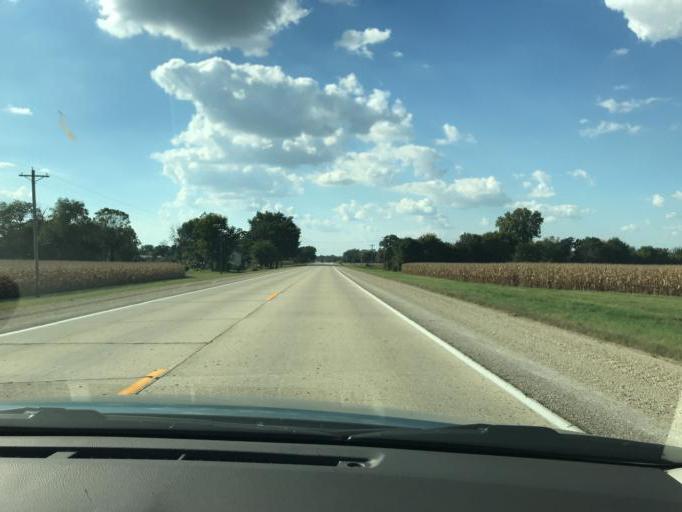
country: US
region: Wisconsin
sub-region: Green County
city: Brodhead
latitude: 42.5654
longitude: -89.3344
